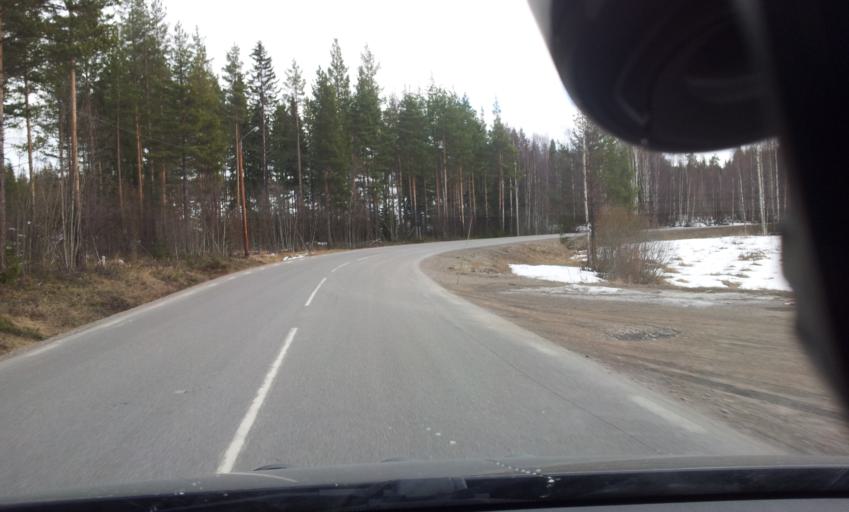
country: SE
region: Vaesternorrland
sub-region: Ange Kommun
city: Ange
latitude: 62.1659
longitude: 15.6777
